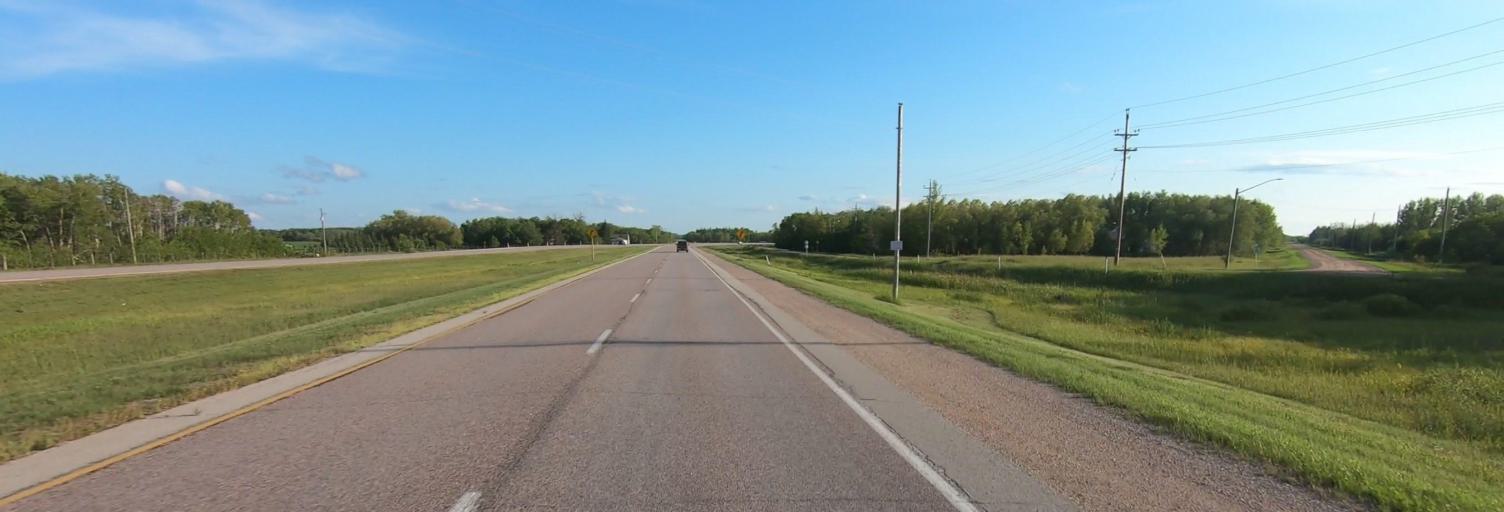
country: CA
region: Manitoba
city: Selkirk
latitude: 50.0920
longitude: -96.8642
